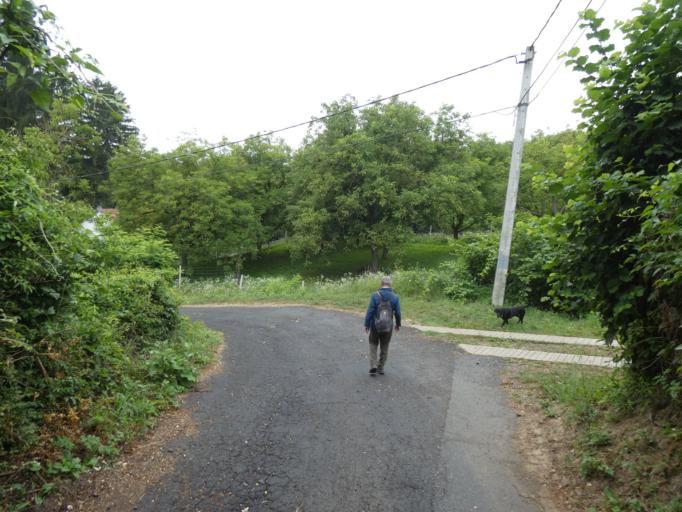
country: HU
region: Pest
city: Szob
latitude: 47.8091
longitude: 18.9031
